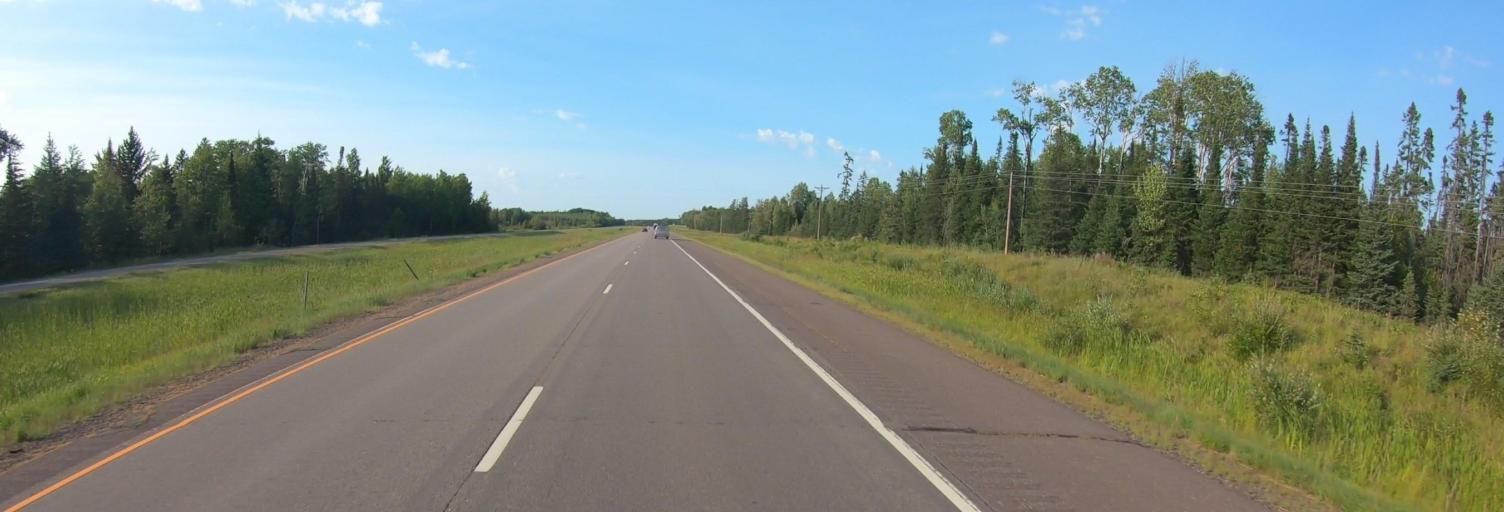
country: US
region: Minnesota
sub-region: Saint Louis County
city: Eveleth
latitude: 47.1159
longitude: -92.4718
